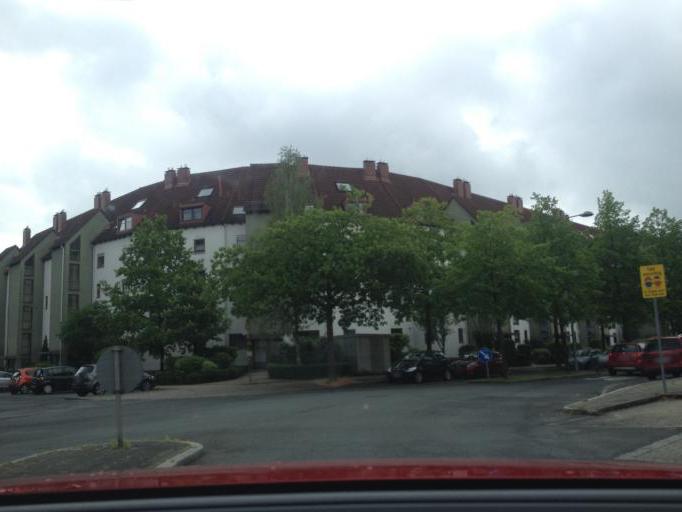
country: DE
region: Bavaria
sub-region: Regierungsbezirk Mittelfranken
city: Rothenbach an der Pegnitz
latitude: 49.4804
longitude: 11.2542
